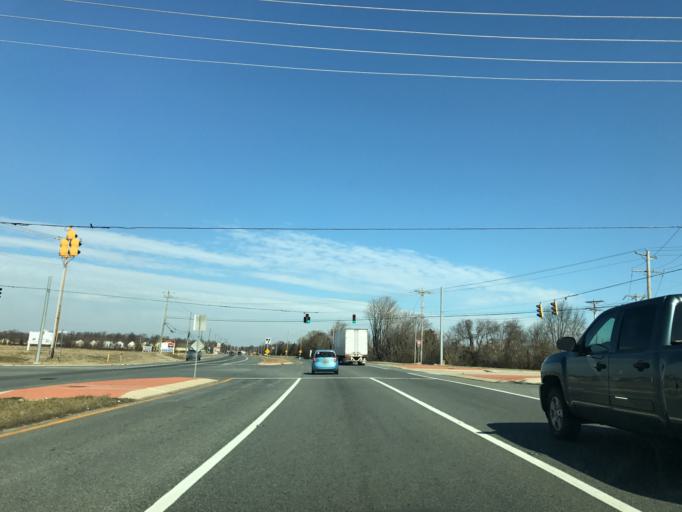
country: US
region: Delaware
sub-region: New Castle County
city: Middletown
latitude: 39.4540
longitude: -75.7235
